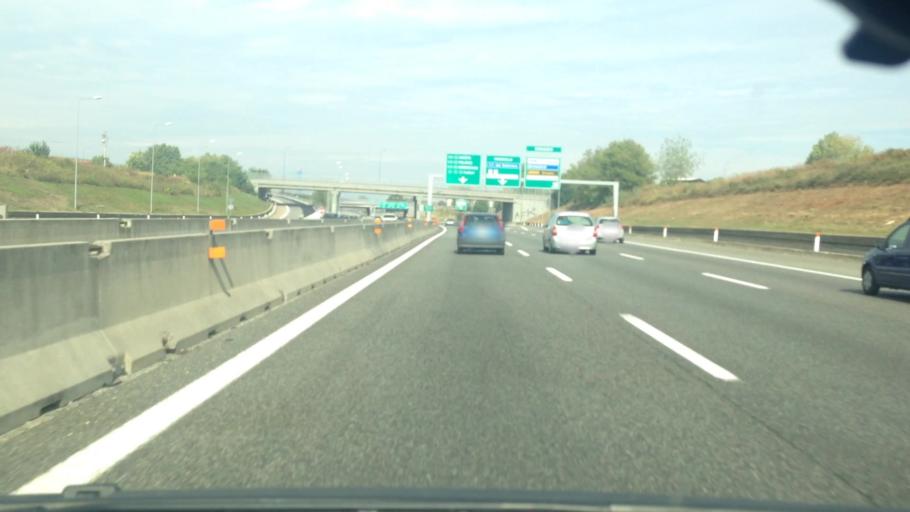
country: IT
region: Piedmont
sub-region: Provincia di Torino
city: Fornaci
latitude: 45.0163
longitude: 7.6019
